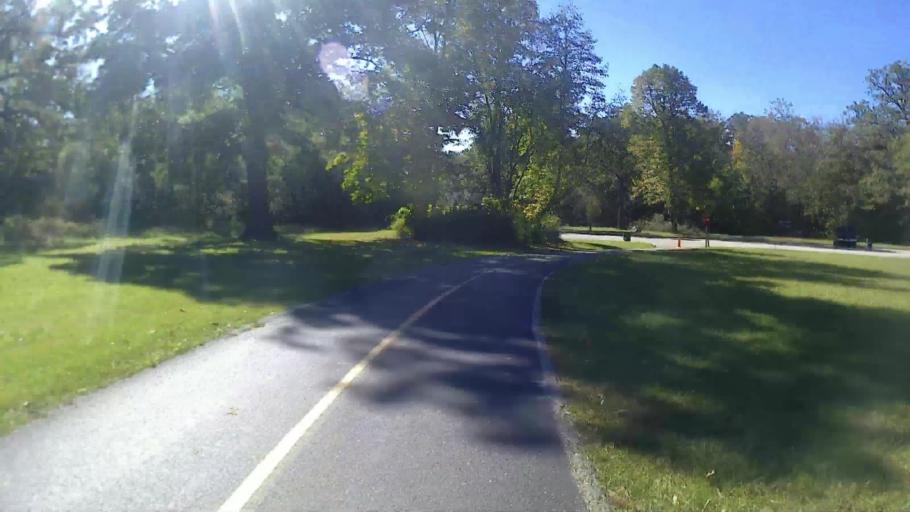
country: US
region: Illinois
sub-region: Cook County
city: Elk Grove Village
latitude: 42.0163
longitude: -87.9955
